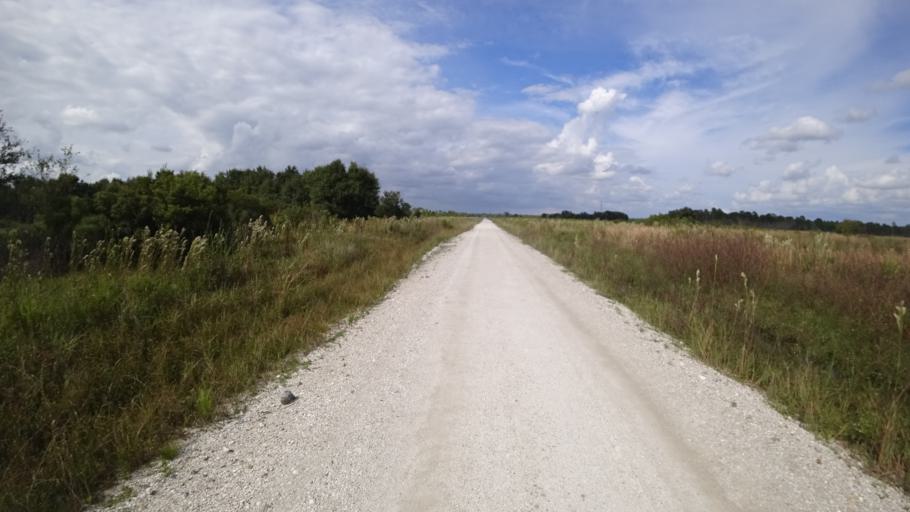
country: US
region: Florida
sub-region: Hillsborough County
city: Wimauma
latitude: 27.5308
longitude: -82.1286
